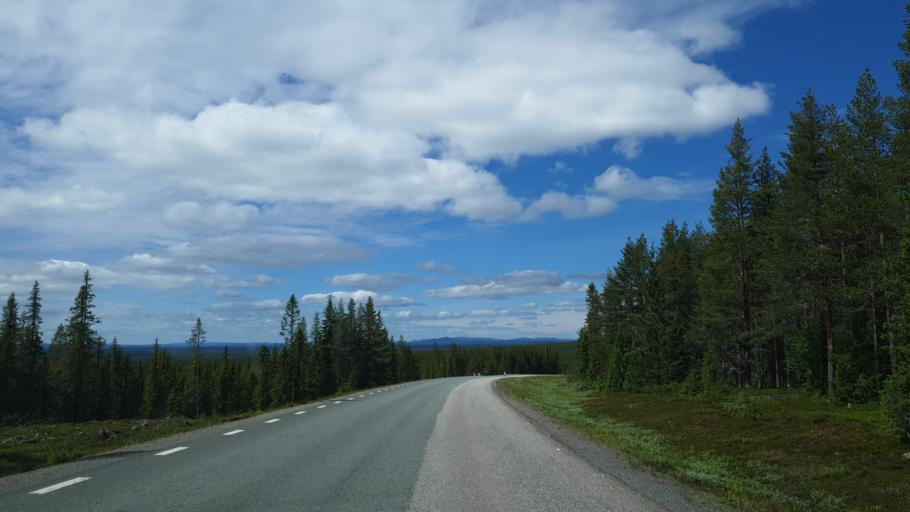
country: SE
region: Vaesterbotten
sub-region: Mala Kommun
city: Mala
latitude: 65.5714
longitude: 18.3529
